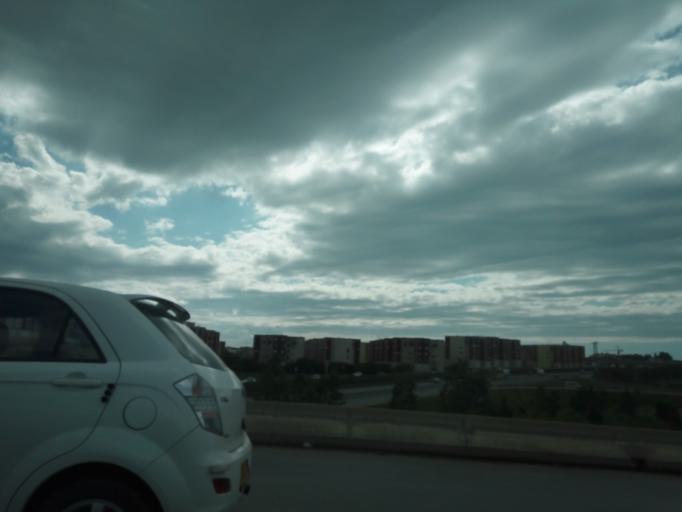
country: DZ
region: Tipaza
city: Douera
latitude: 36.6856
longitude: 2.9568
